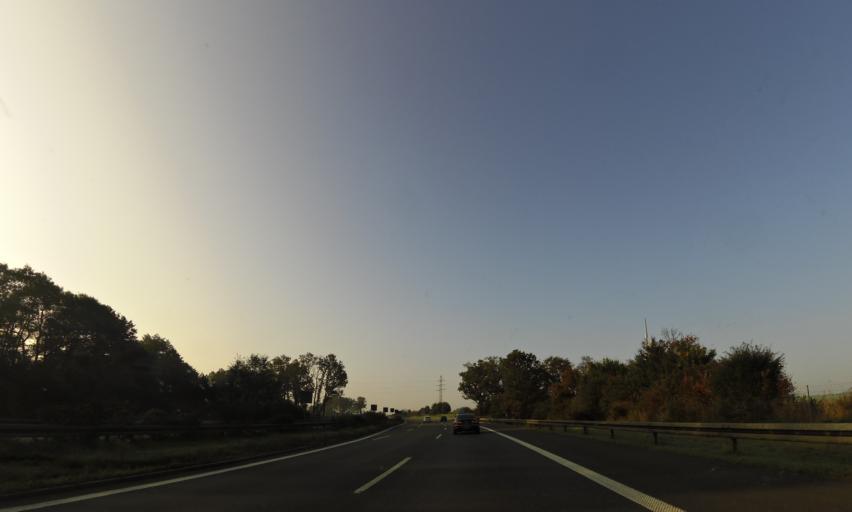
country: DE
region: Saxony
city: Treuen
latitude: 50.5721
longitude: 12.2859
